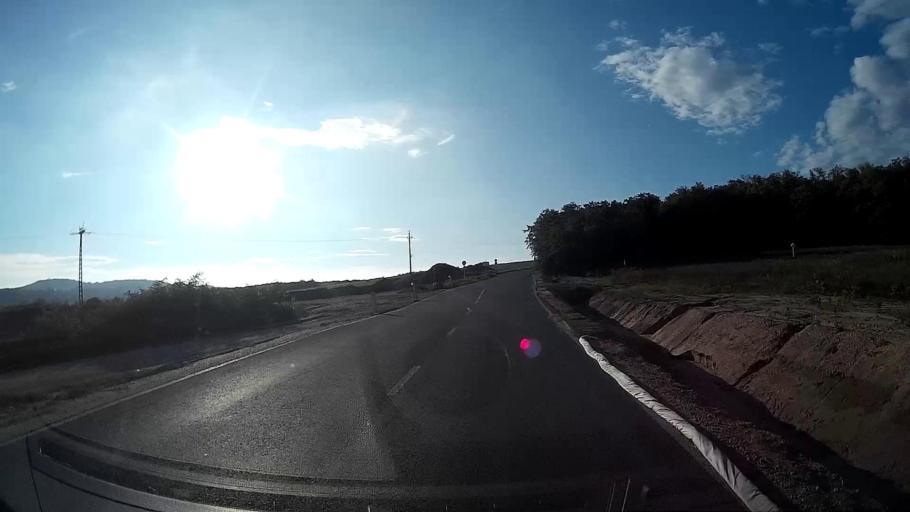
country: HU
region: Pest
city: Mogyorod
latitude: 47.5901
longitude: 19.2305
